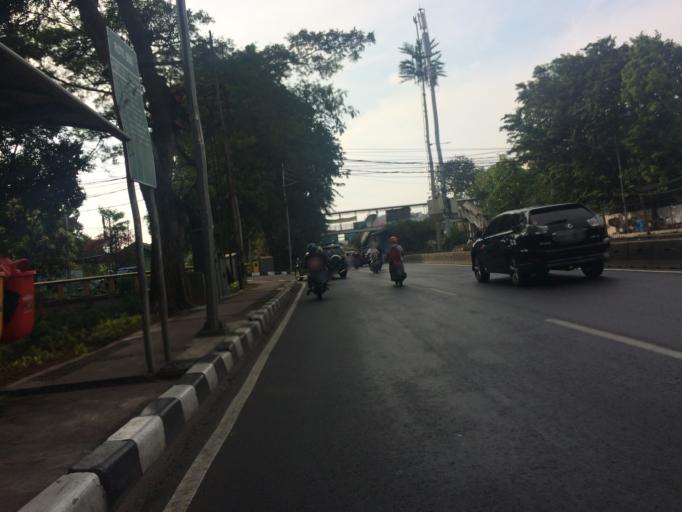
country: ID
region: Jakarta Raya
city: Jakarta
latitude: -6.1695
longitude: 106.8398
